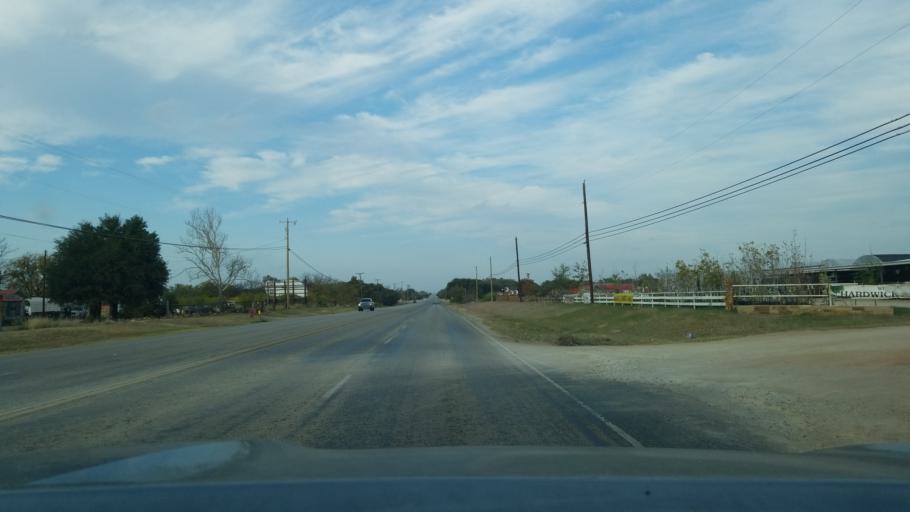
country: US
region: Texas
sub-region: Brown County
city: Early
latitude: 31.7529
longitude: -98.9614
